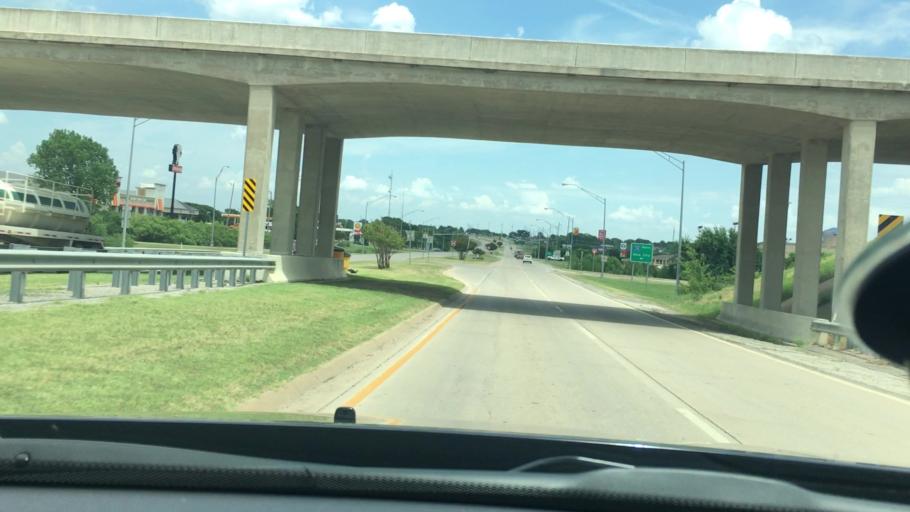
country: US
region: Oklahoma
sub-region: Carter County
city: Ardmore
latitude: 34.2020
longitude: -97.1642
